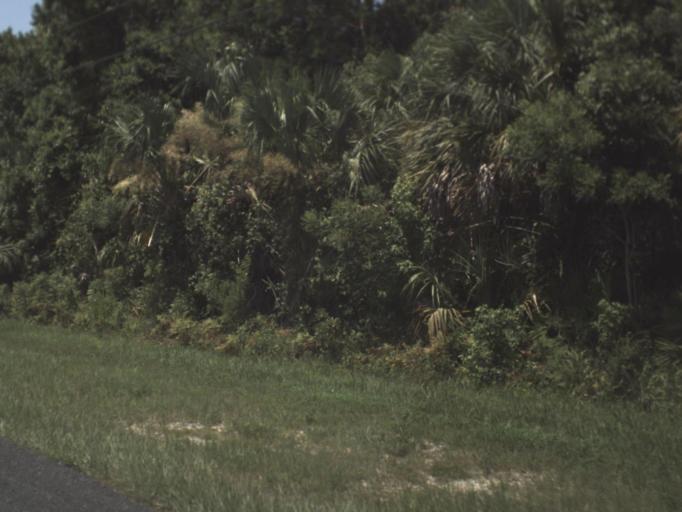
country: US
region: Florida
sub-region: Citrus County
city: Homosassa Springs
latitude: 28.8310
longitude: -82.5795
